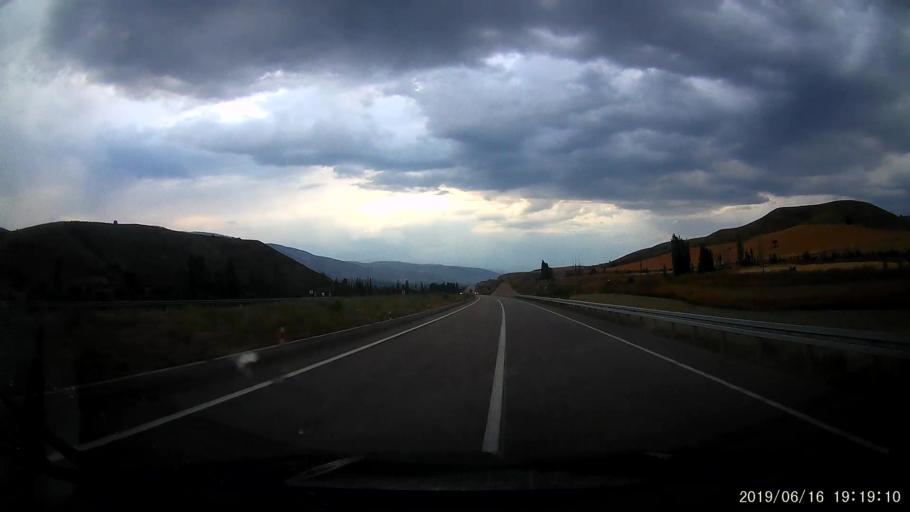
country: TR
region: Sivas
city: Akincilar
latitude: 40.0941
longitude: 38.4376
